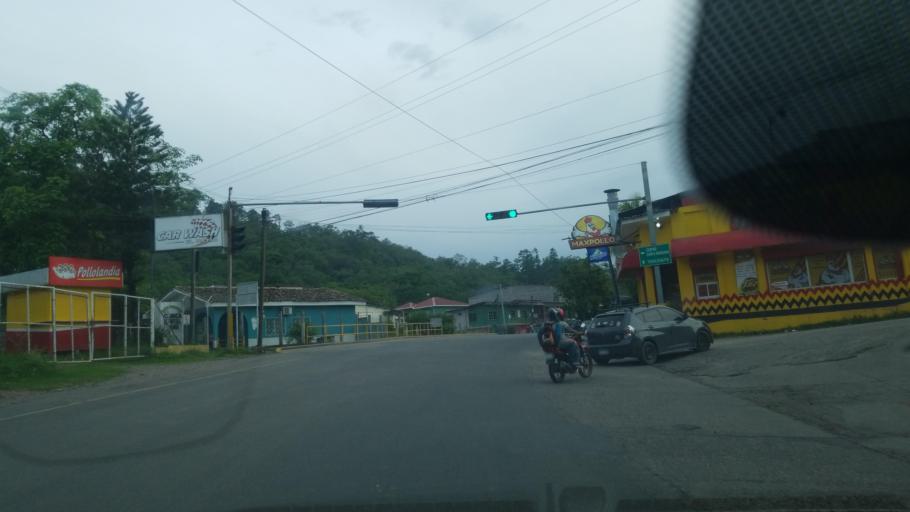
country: HN
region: Santa Barbara
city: Santa Barbara
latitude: 14.9212
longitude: -88.2406
